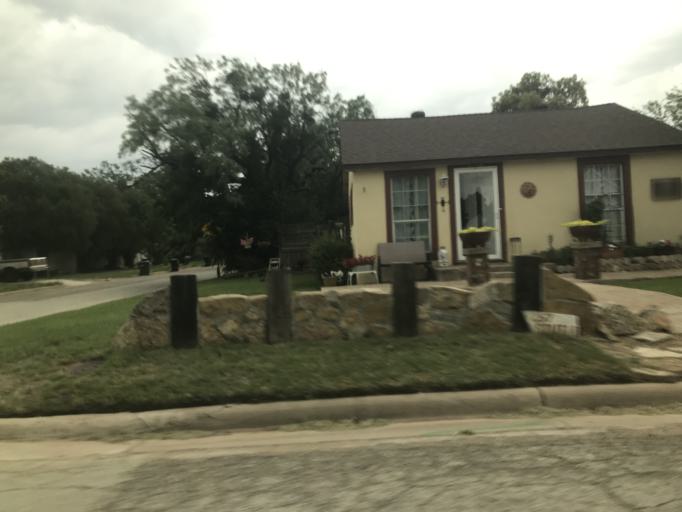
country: US
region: Texas
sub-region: Taylor County
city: Abilene
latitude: 32.4483
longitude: -99.7555
